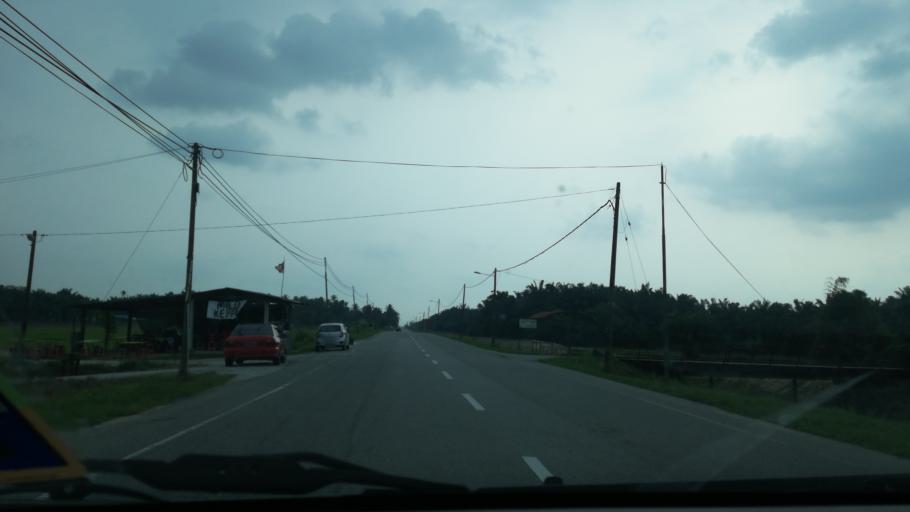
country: MY
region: Perak
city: Teluk Intan
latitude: 4.1176
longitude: 101.0751
